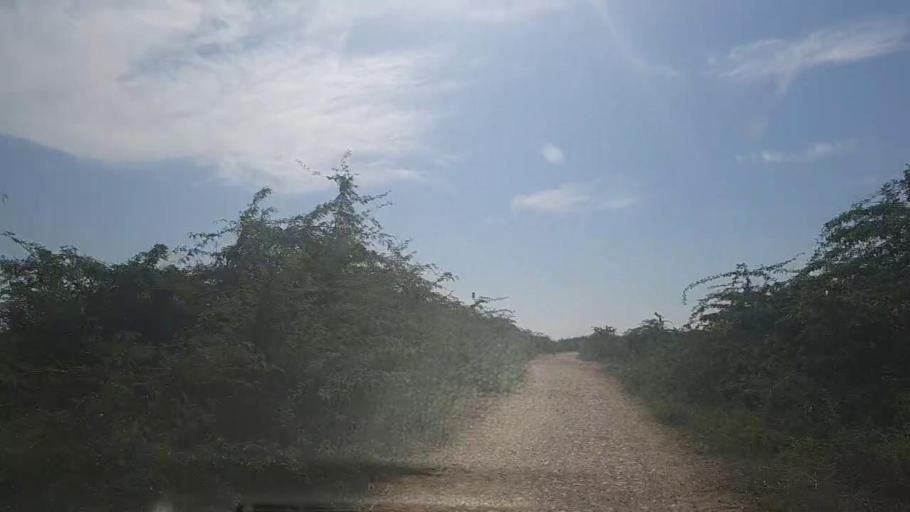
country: PK
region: Sindh
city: Mirpur Batoro
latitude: 24.6795
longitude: 68.1821
